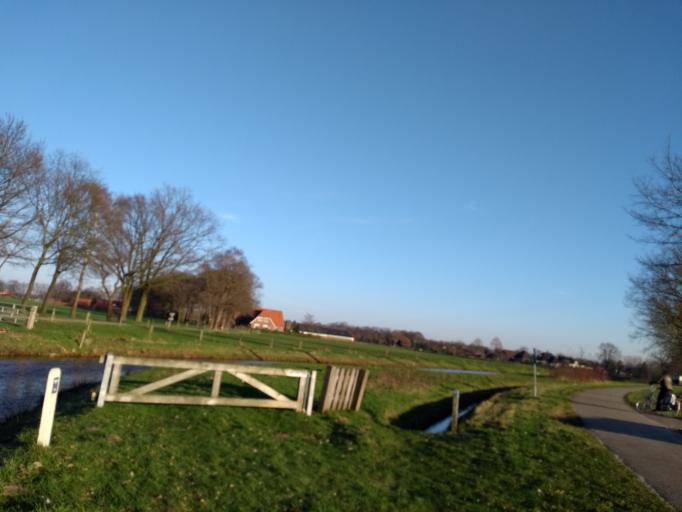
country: NL
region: Overijssel
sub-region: Gemeente Almelo
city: Almelo
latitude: 52.3764
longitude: 6.7136
